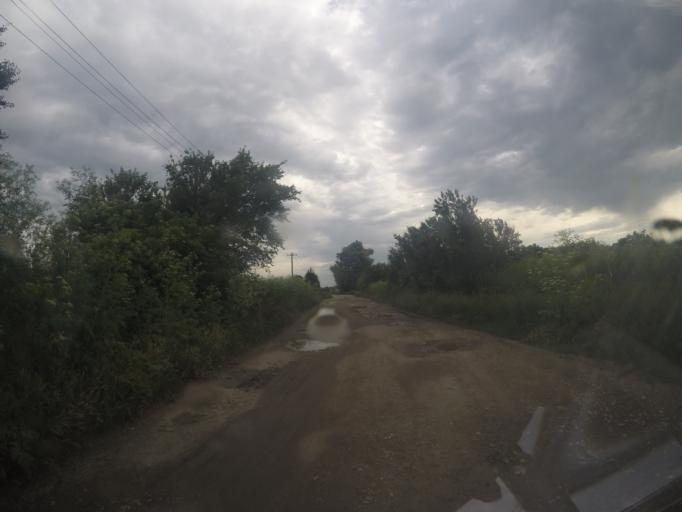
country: RS
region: Central Serbia
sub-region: Belgrade
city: Zemun
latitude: 44.8814
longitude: 20.3835
